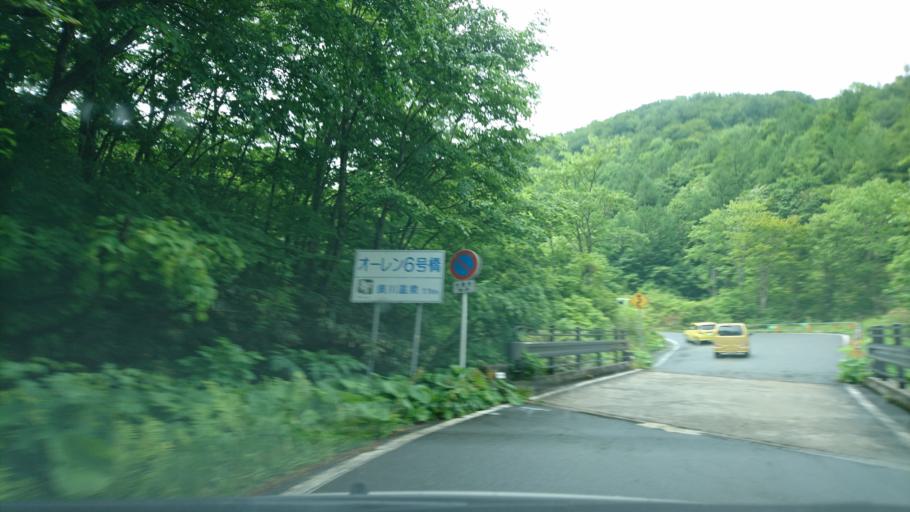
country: JP
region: Iwate
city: Ichinoseki
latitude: 38.9949
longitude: 140.8222
